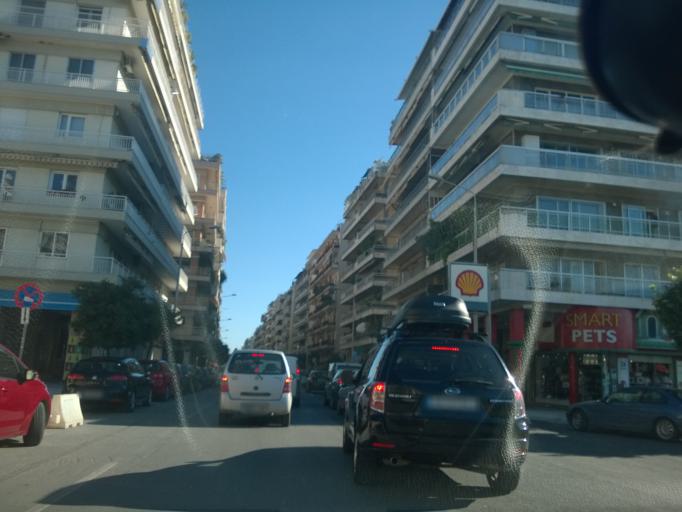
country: GR
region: Central Macedonia
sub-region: Nomos Thessalonikis
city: Kalamaria
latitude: 40.6015
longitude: 22.9509
